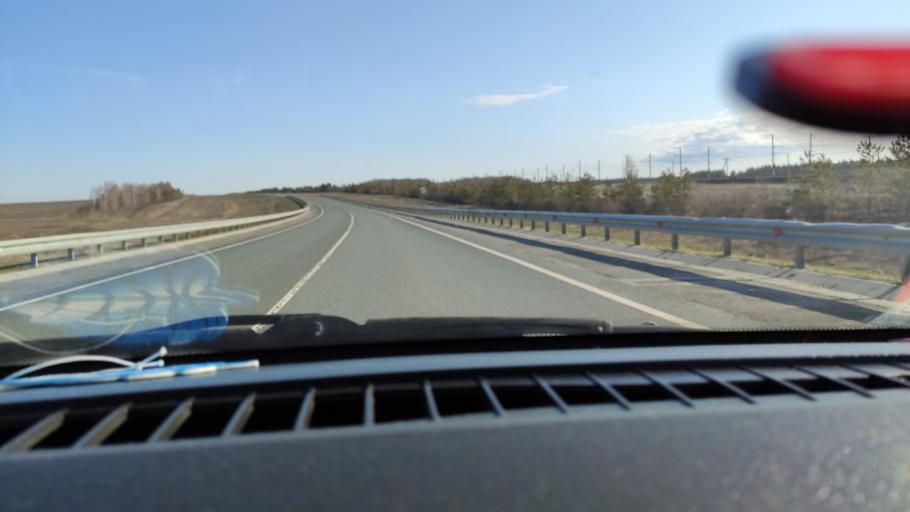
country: RU
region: Samara
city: Syzran'
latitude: 52.8746
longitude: 48.2888
